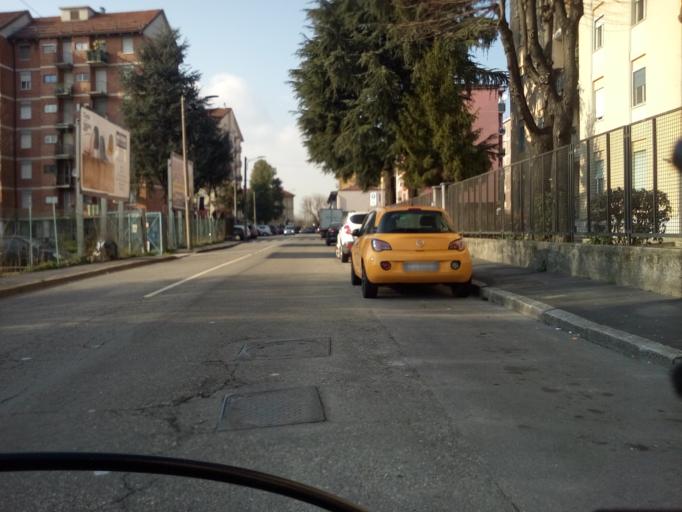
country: IT
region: Lombardy
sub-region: Citta metropolitana di Milano
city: Cesano Boscone
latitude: 45.4660
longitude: 9.0856
